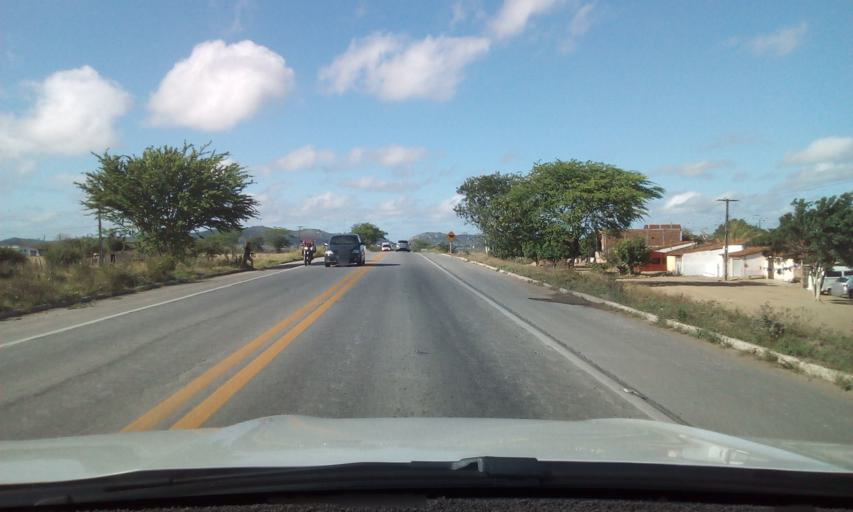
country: BR
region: Paraiba
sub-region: Campina Grande
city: Campina Grande
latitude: -7.3053
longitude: -35.8930
